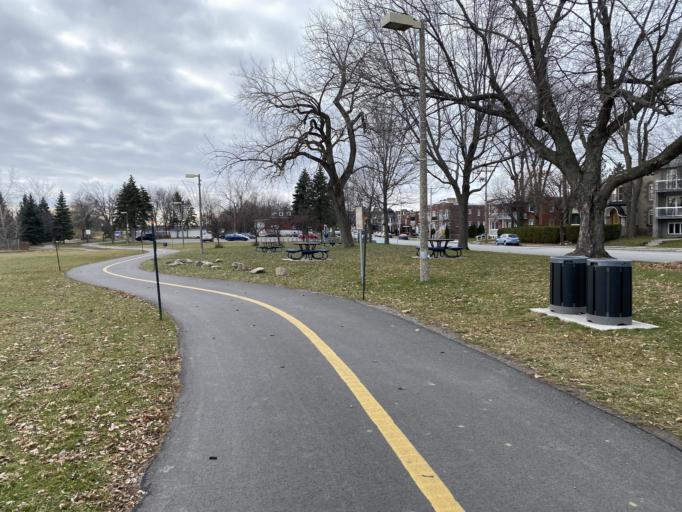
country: CA
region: Quebec
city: Saint-Raymond
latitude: 45.4302
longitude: -73.5921
